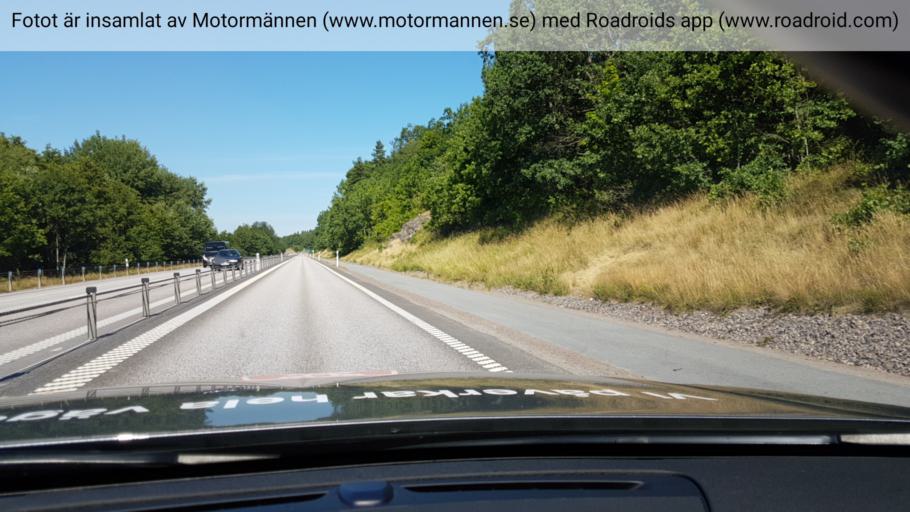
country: SE
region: OEstergoetland
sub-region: Finspangs Kommun
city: Finspang
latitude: 58.7025
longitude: 15.8827
